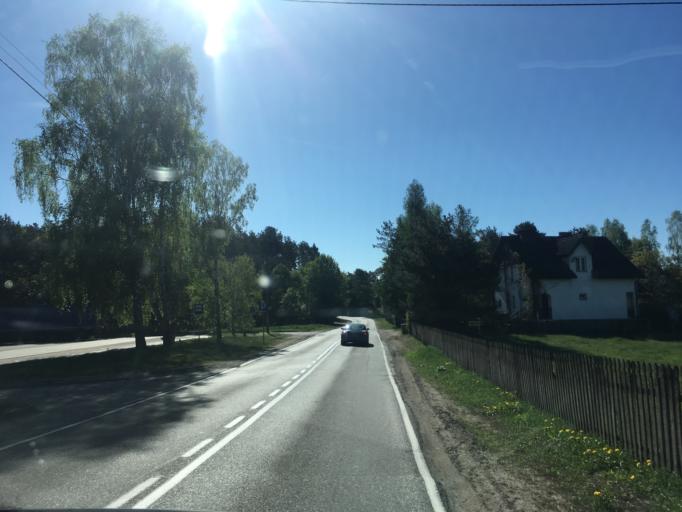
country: PL
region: Warmian-Masurian Voivodeship
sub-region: Powiat szczycienski
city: Jedwabno
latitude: 53.5392
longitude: 20.7884
